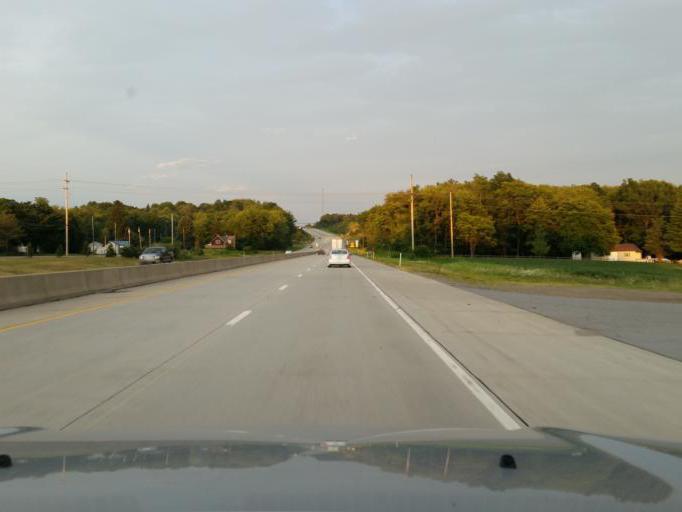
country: US
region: Pennsylvania
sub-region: Indiana County
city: Black Lick
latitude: 40.4465
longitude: -79.0965
